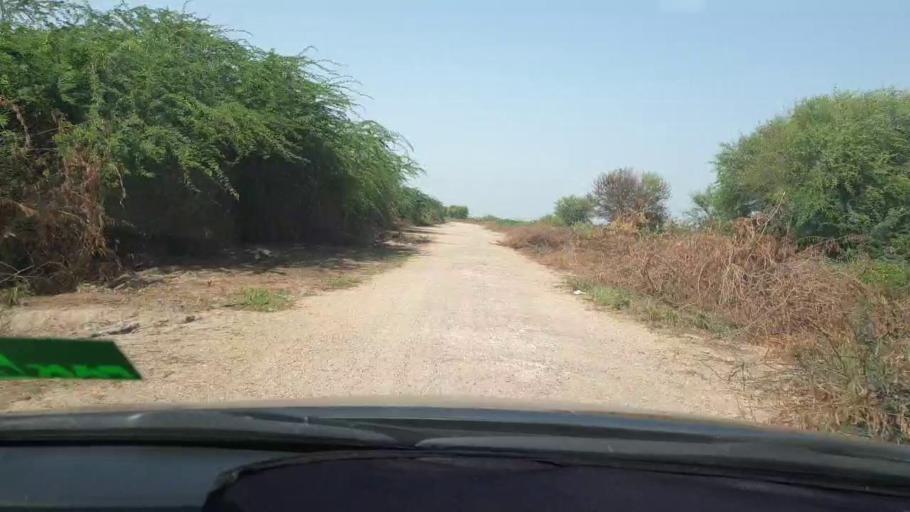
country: PK
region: Sindh
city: Digri
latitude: 24.9379
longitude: 69.1465
